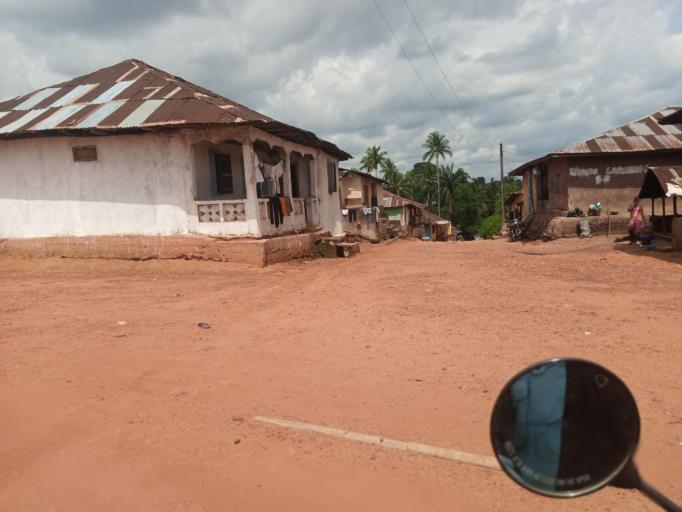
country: SL
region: Southern Province
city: Bo
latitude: 7.9746
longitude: -11.7381
